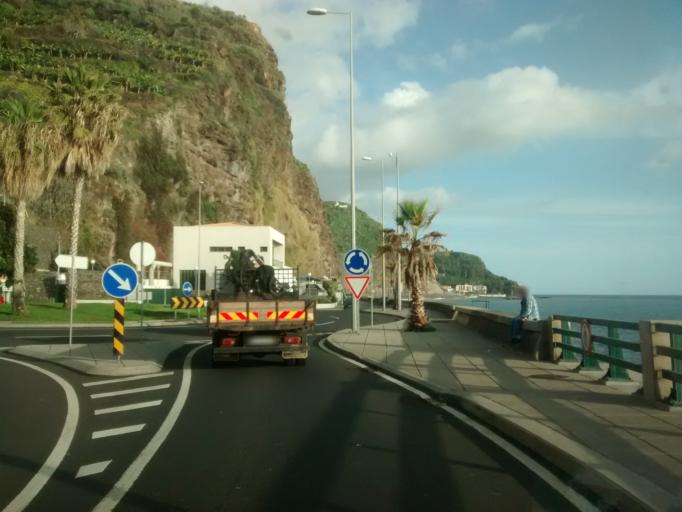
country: PT
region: Madeira
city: Ponta do Sol
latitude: 32.6772
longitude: -17.0789
